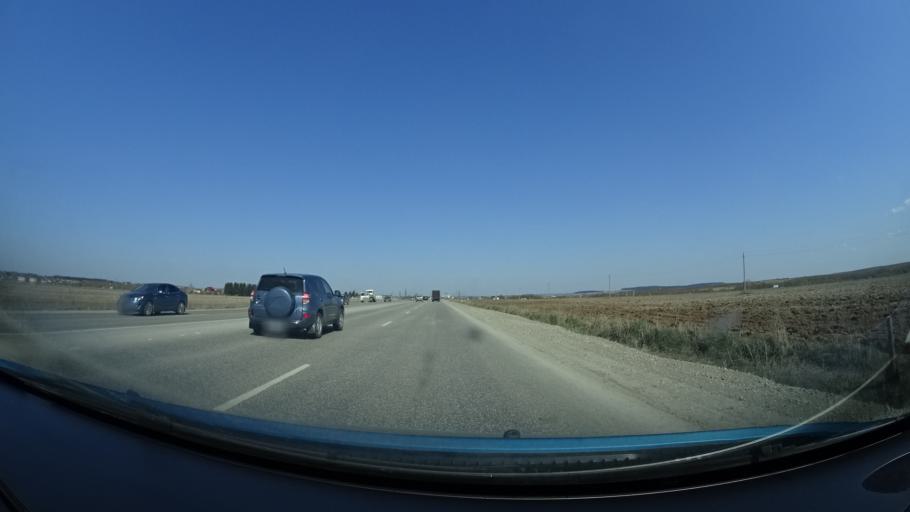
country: RU
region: Perm
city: Kultayevo
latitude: 57.8809
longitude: 55.9152
